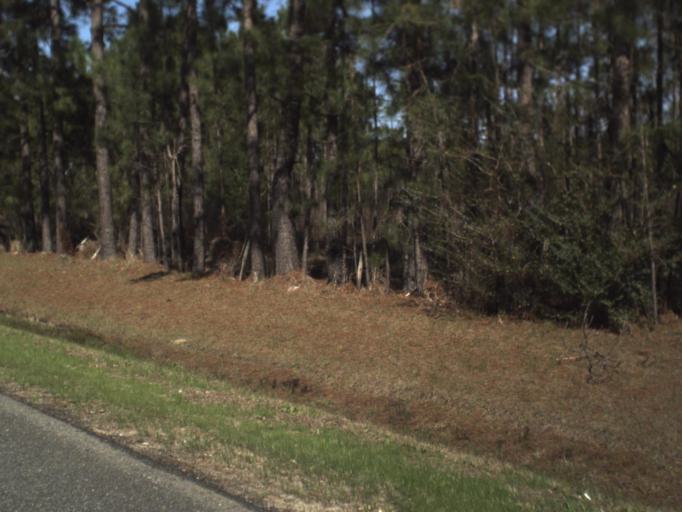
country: US
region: Florida
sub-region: Calhoun County
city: Blountstown
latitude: 30.4006
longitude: -85.0870
